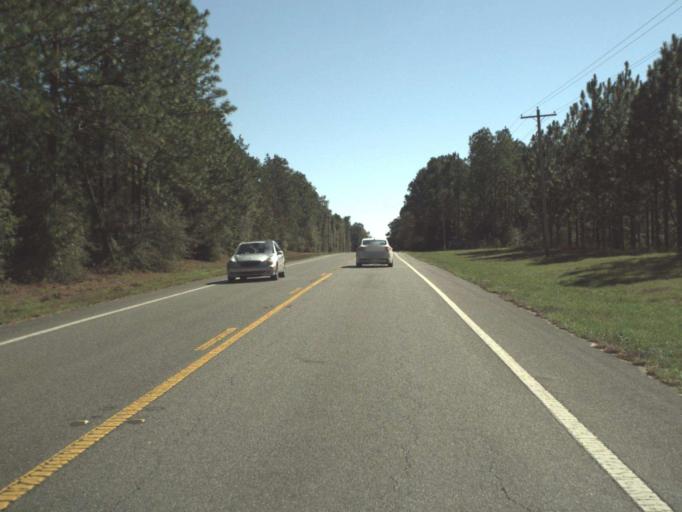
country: US
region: Florida
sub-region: Okaloosa County
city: Crestview
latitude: 30.8249
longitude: -86.7241
